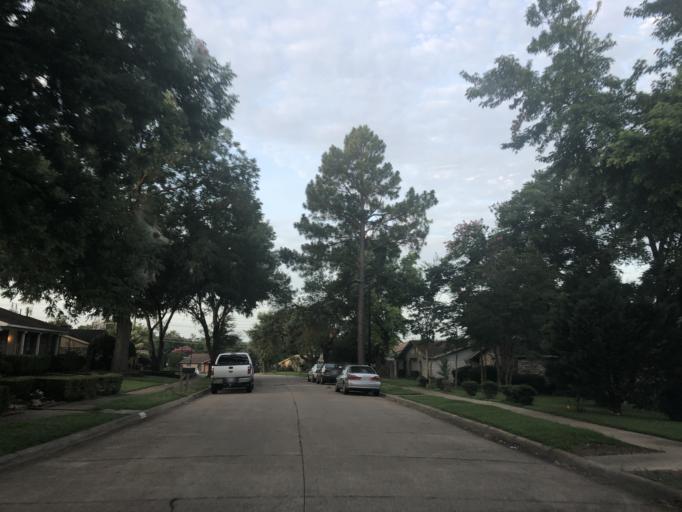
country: US
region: Texas
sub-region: Dallas County
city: Sunnyvale
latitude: 32.8358
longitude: -96.5939
